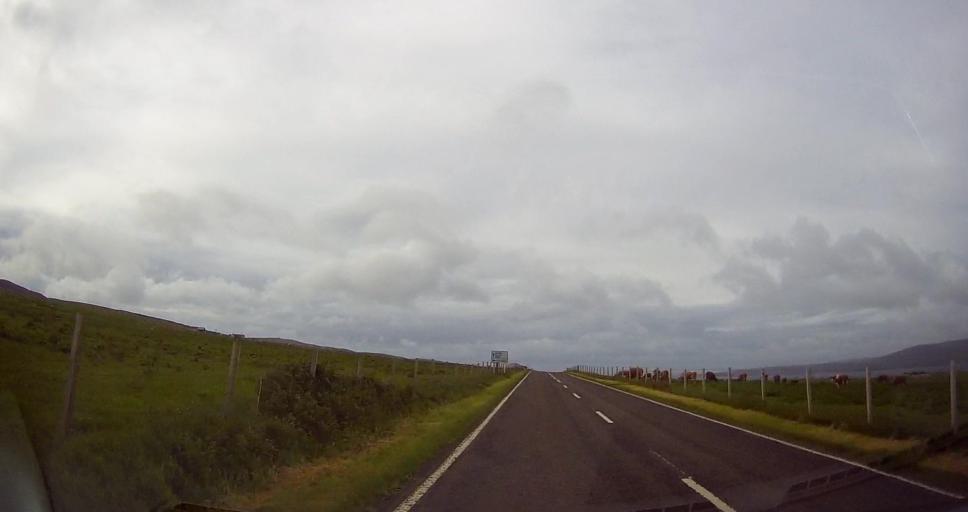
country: GB
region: Scotland
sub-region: Orkney Islands
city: Stromness
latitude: 58.9478
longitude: -3.2154
